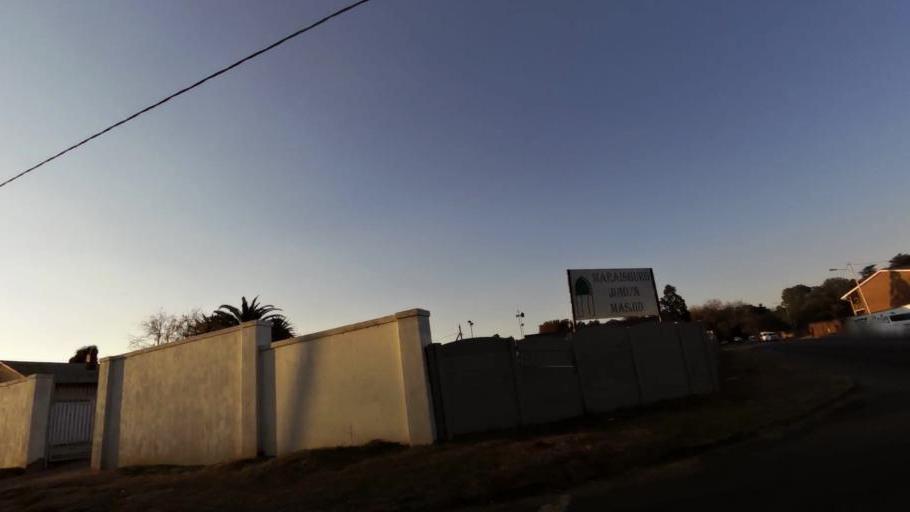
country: ZA
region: Gauteng
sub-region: City of Johannesburg Metropolitan Municipality
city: Roodepoort
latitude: -26.1819
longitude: 27.9403
